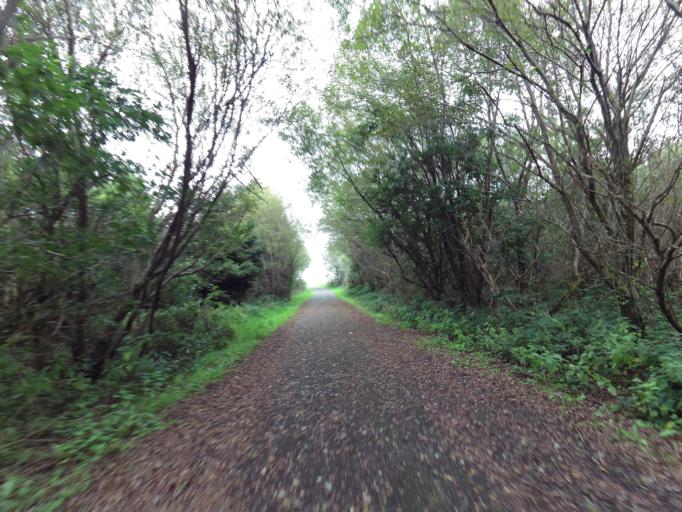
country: IE
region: Leinster
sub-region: Uibh Fhaili
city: Ferbane
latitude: 53.2119
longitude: -7.7307
